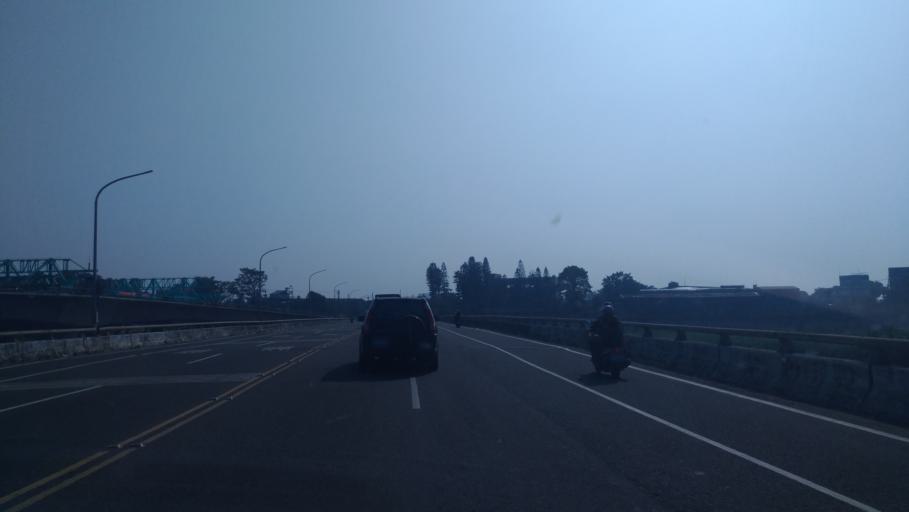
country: TW
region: Taiwan
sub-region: Chiayi
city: Jiayi Shi
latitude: 23.5102
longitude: 120.4332
